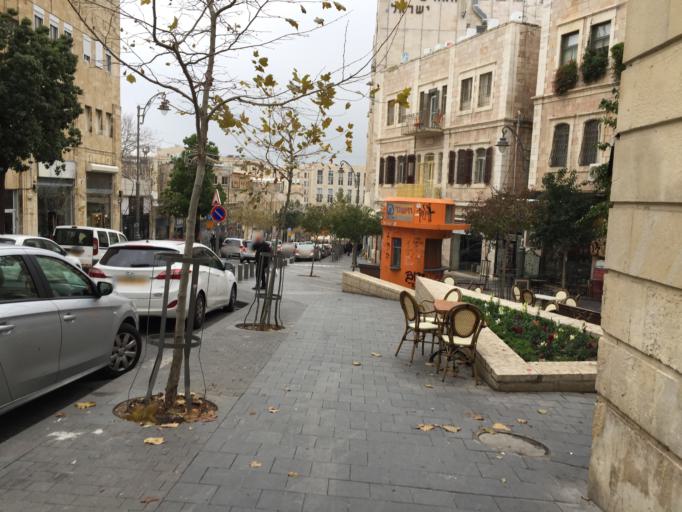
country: IL
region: Jerusalem
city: West Jerusalem
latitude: 31.7798
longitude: 35.2219
